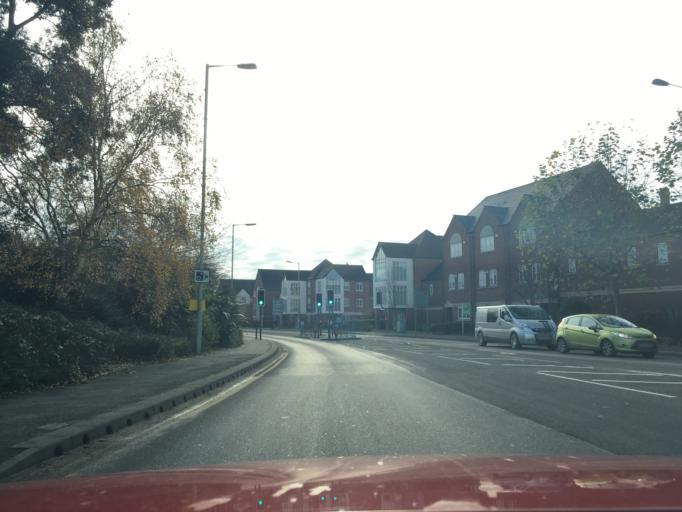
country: GB
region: England
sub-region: Staffordshire
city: Burton upon Trent
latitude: 52.8021
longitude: -1.6438
